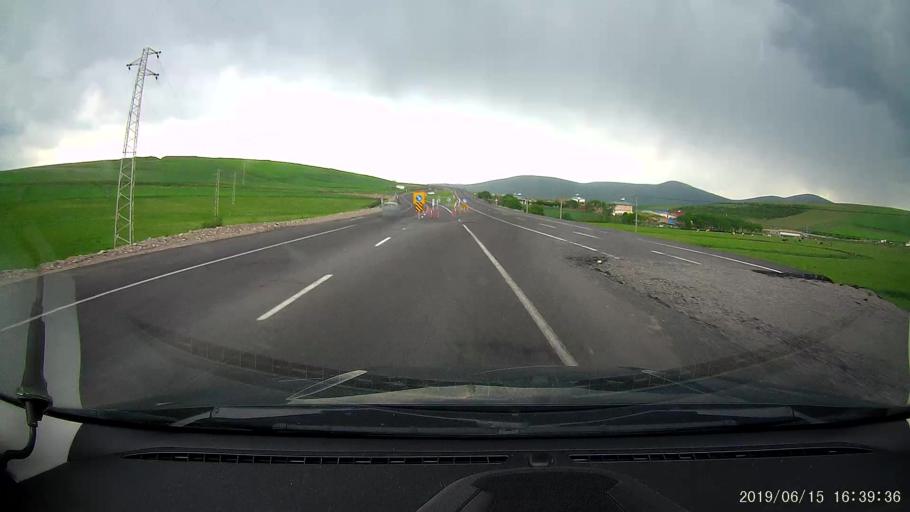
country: TR
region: Ardahan
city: Haskoy
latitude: 40.9812
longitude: 42.8966
